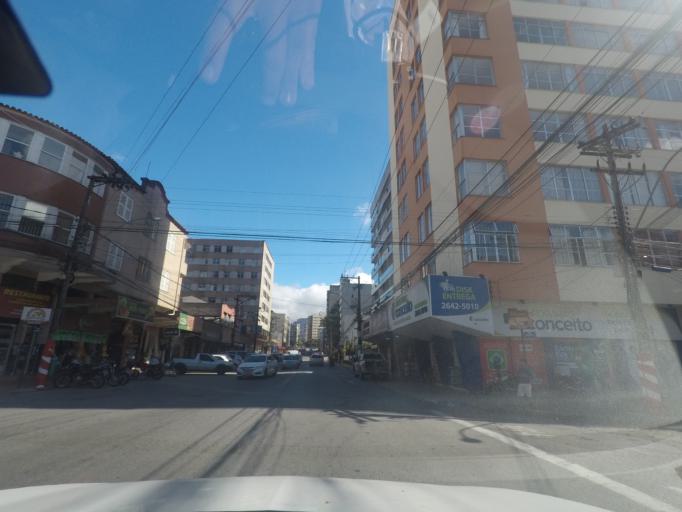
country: BR
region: Rio de Janeiro
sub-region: Teresopolis
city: Teresopolis
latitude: -22.4380
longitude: -42.9793
